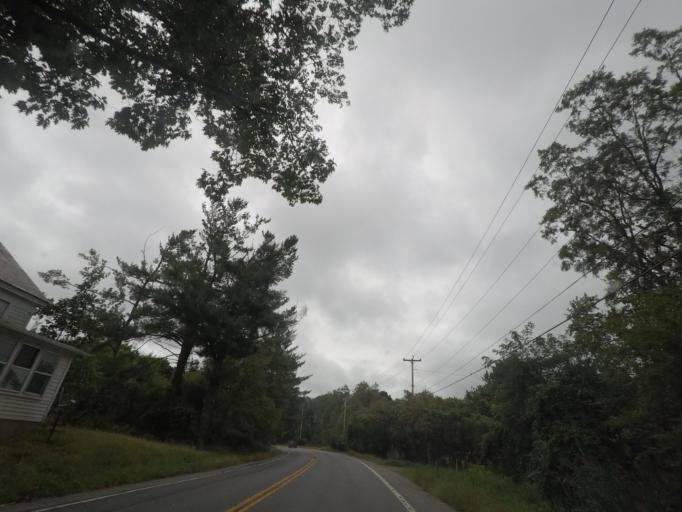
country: US
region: New York
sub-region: Saratoga County
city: Country Knolls
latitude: 42.9326
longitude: -73.7678
